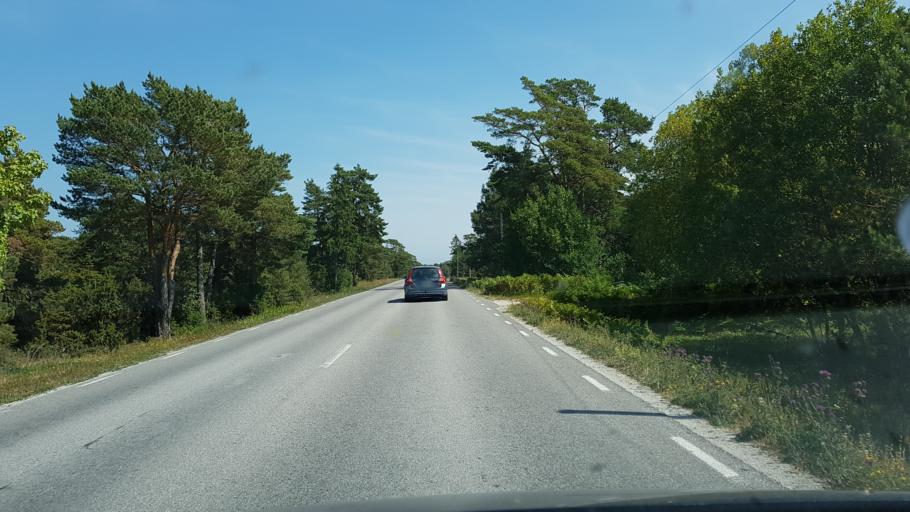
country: SE
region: Gotland
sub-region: Gotland
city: Visby
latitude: 57.6314
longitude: 18.4178
